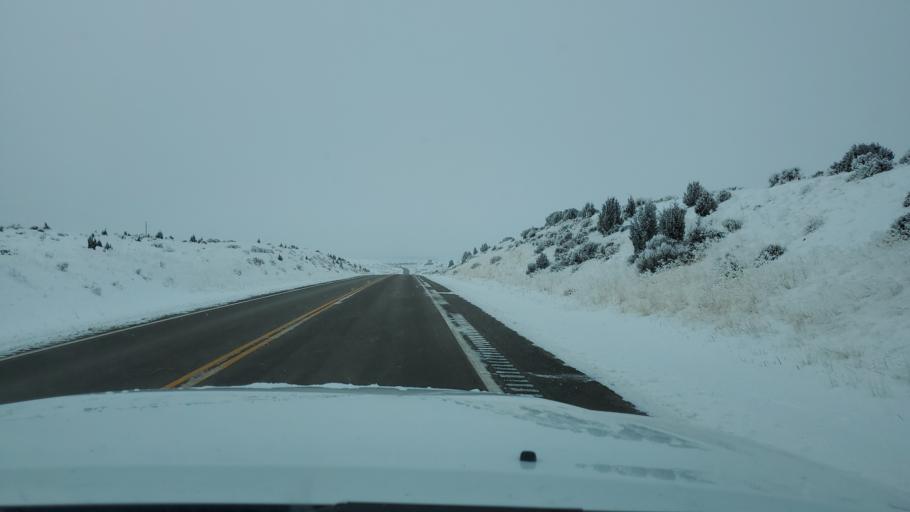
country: US
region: Colorado
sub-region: Rio Blanco County
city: Rangely
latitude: 40.3380
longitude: -108.4747
